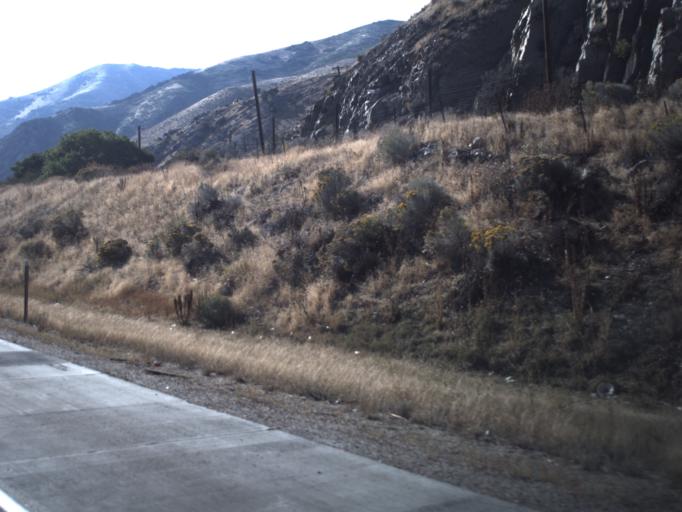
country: US
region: Utah
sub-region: Morgan County
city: Morgan
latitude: 41.0625
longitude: -111.5648
